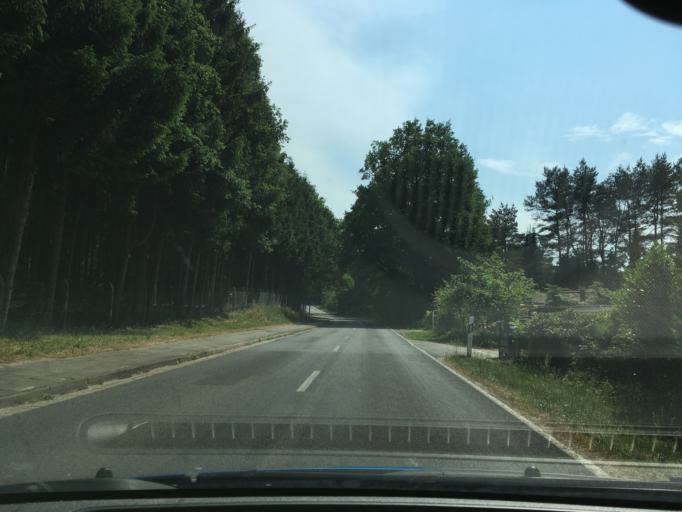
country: DE
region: Lower Saxony
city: Jesteburg
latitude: 53.2807
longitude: 9.9141
